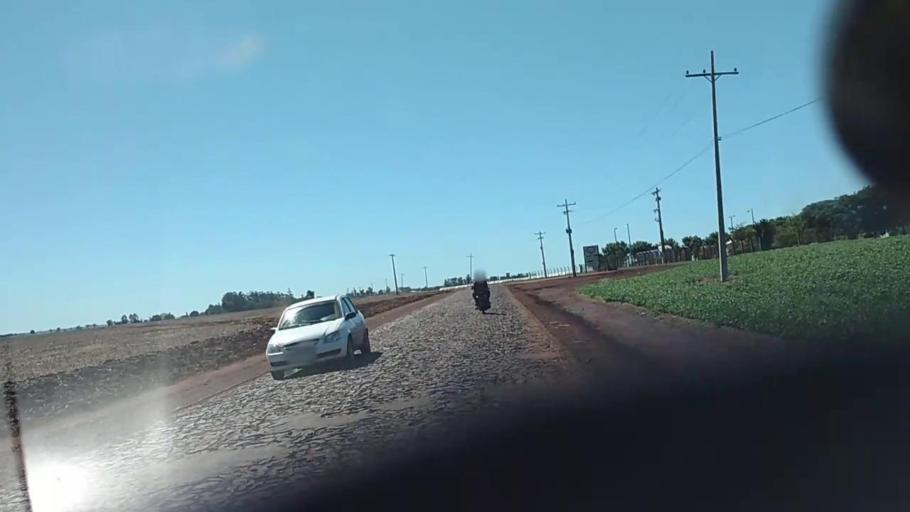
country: PY
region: Alto Parana
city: Naranjal
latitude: -25.9708
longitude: -55.1511
